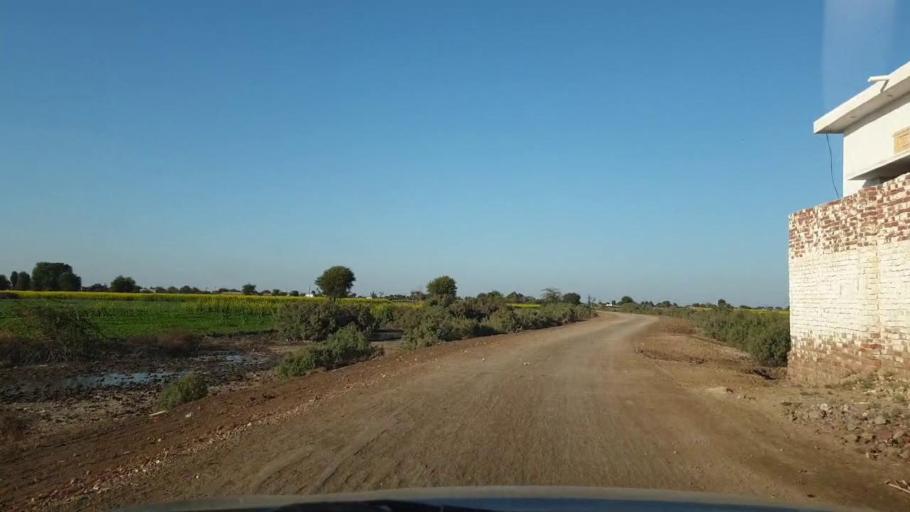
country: PK
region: Sindh
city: Jhol
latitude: 25.9135
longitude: 68.9253
